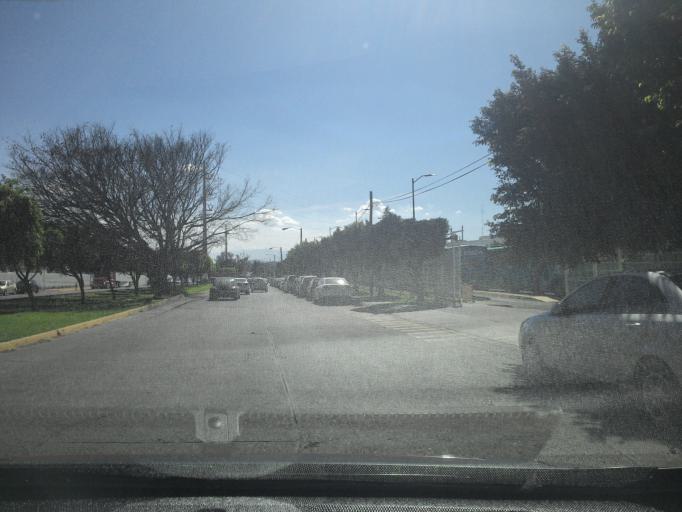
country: MX
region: Jalisco
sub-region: Zapopan
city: Zapopan
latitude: 20.7431
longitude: -103.3994
